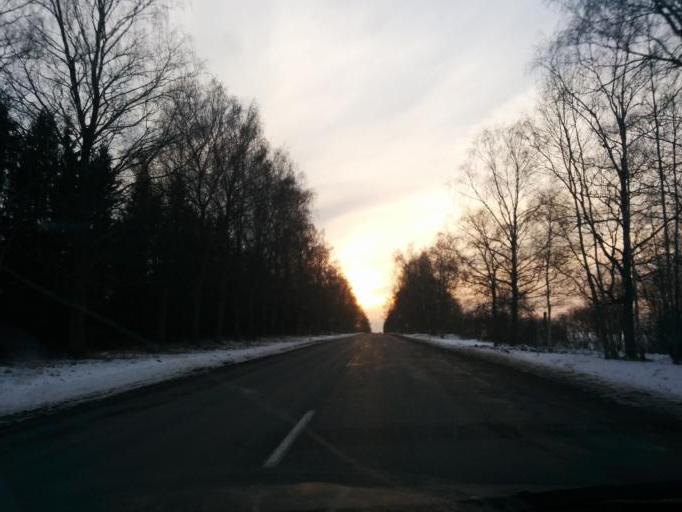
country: LV
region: Priekuli
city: Priekuli
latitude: 57.2589
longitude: 25.3943
